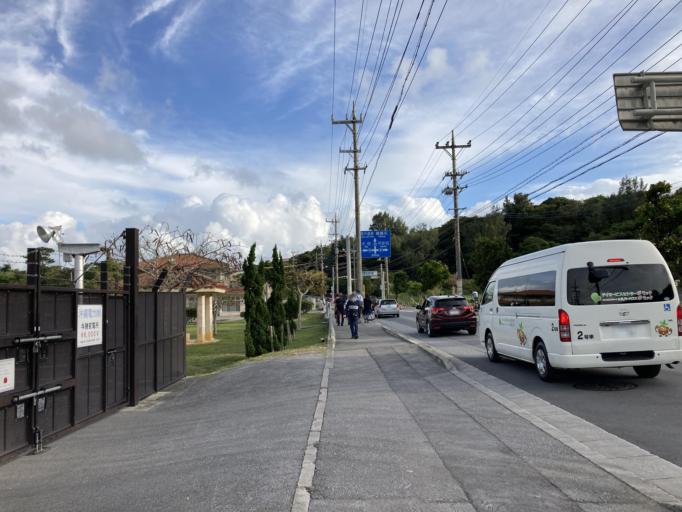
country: JP
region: Okinawa
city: Katsuren-haebaru
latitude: 26.3315
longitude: 127.8805
